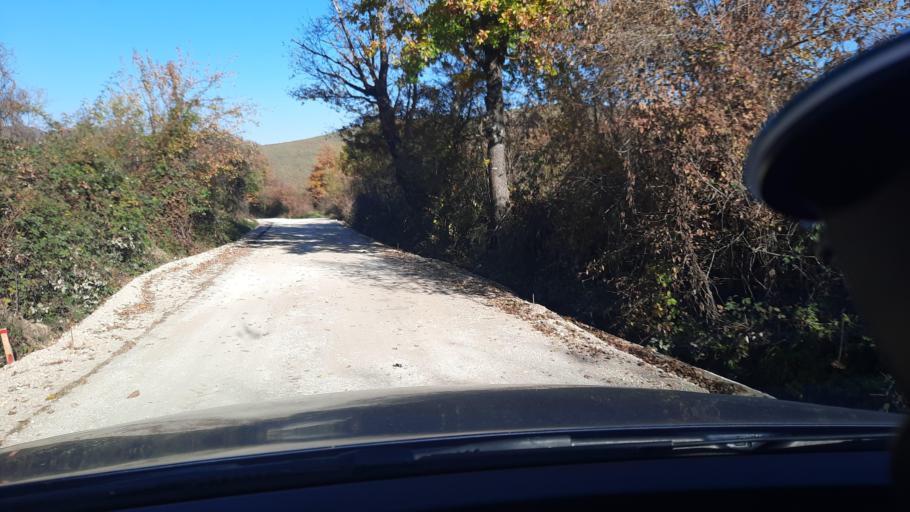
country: MK
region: Demir Hisar
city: Sopotnica
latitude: 41.2696
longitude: 21.0843
